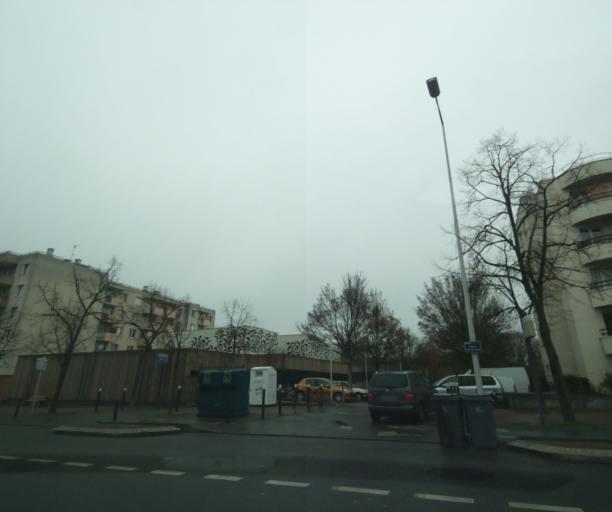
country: FR
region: Ile-de-France
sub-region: Departement des Hauts-de-Seine
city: Nanterre
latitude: 48.8909
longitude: 2.2158
